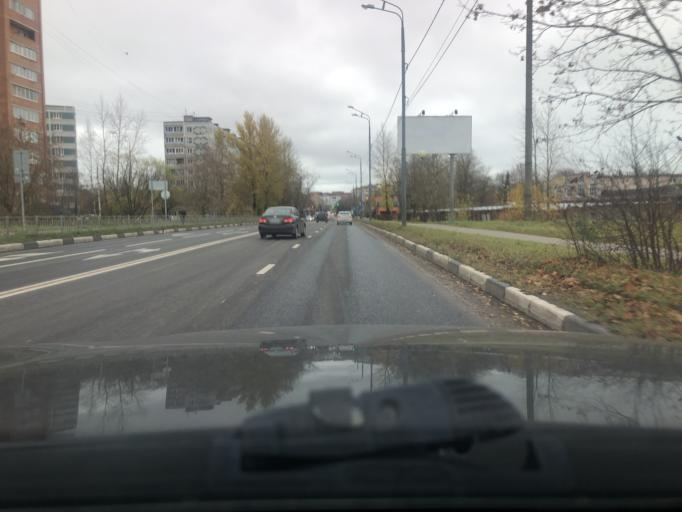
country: RU
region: Moskovskaya
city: Sergiyev Posad
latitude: 56.3319
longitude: 38.1312
